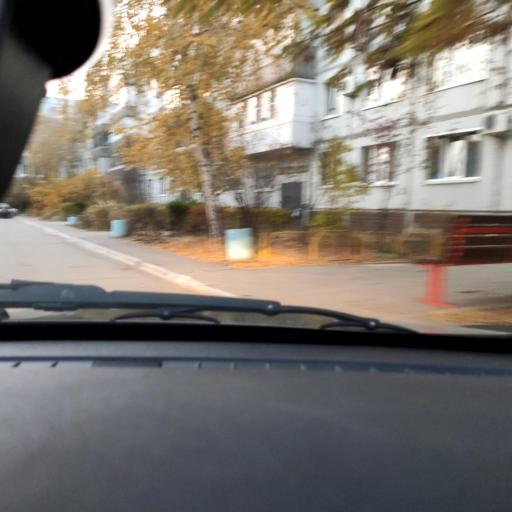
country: RU
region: Samara
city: Tol'yatti
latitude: 53.5289
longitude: 49.2715
